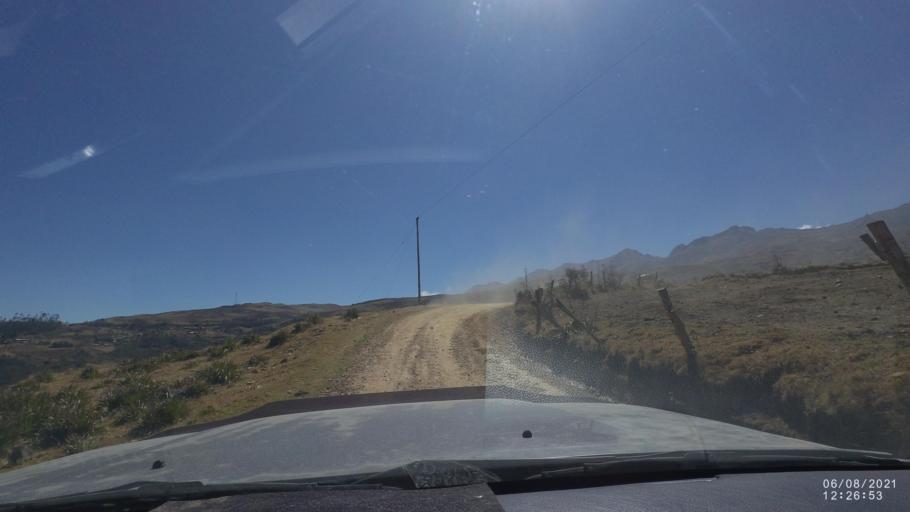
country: BO
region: Cochabamba
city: Colchani
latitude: -16.7913
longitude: -66.6551
